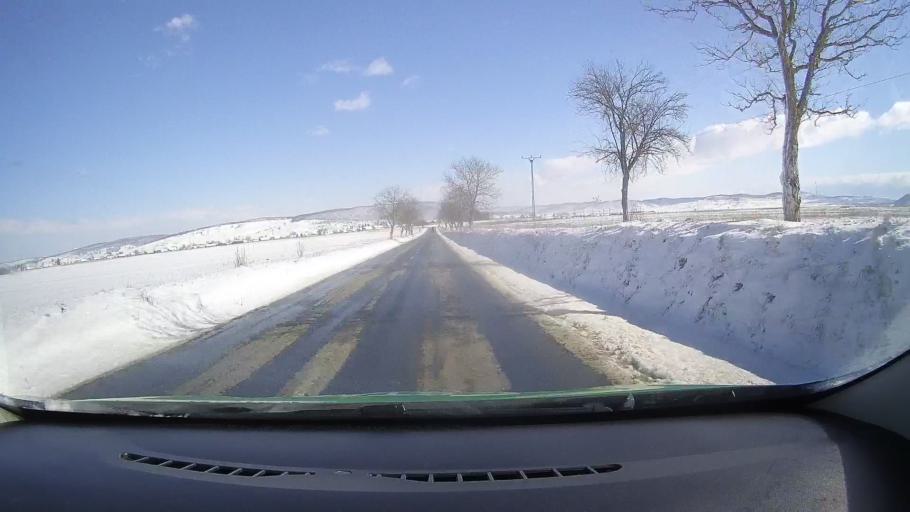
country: RO
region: Sibiu
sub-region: Comuna Rosia
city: Rosia
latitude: 45.8111
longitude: 24.2998
